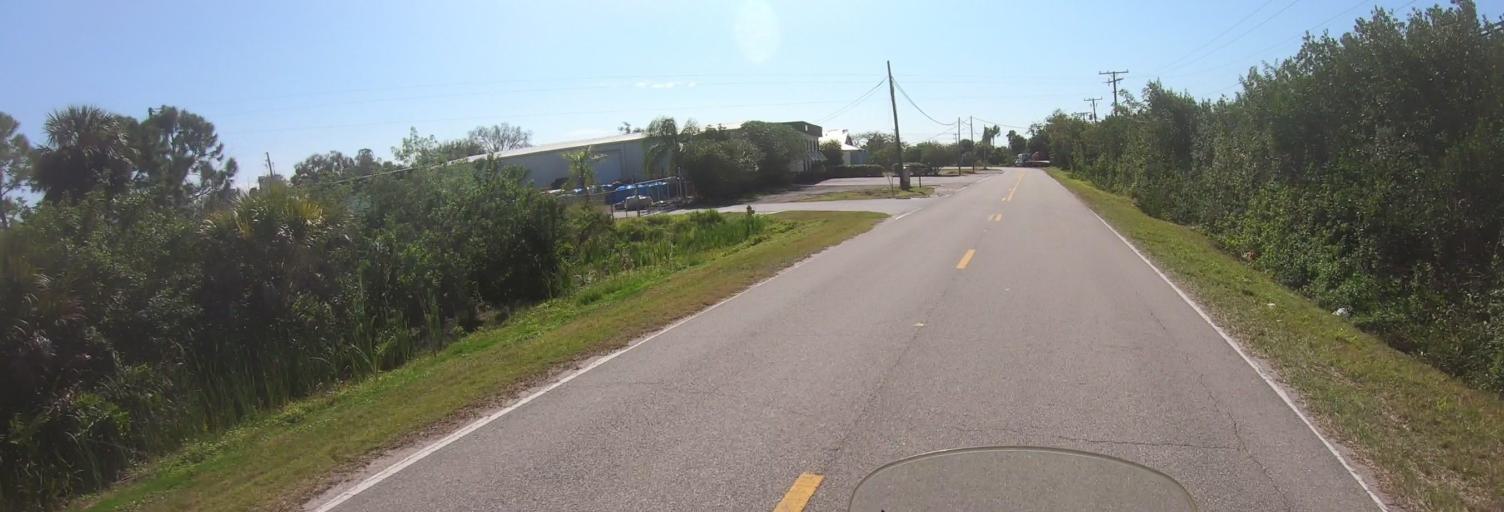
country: US
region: Florida
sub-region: Manatee County
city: Memphis
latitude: 27.5810
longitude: -82.5536
